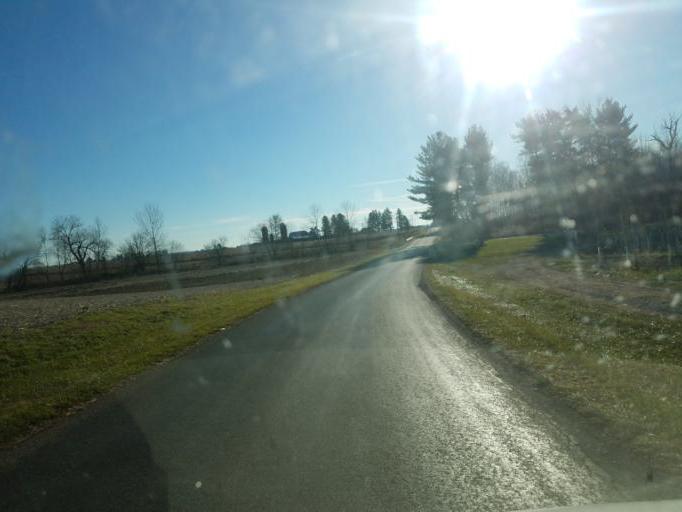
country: US
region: Ohio
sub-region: Knox County
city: Fredericktown
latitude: 40.4558
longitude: -82.5923
